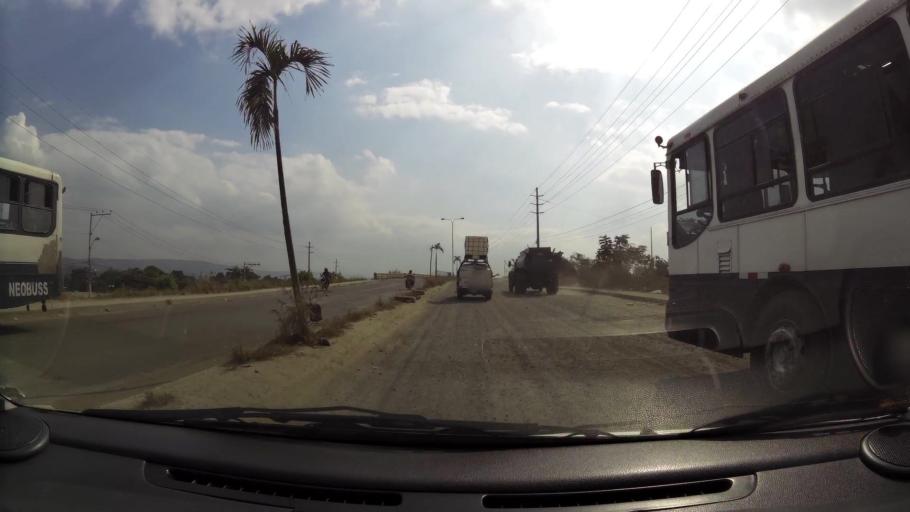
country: EC
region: Guayas
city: Santa Lucia
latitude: -2.1205
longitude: -79.9741
